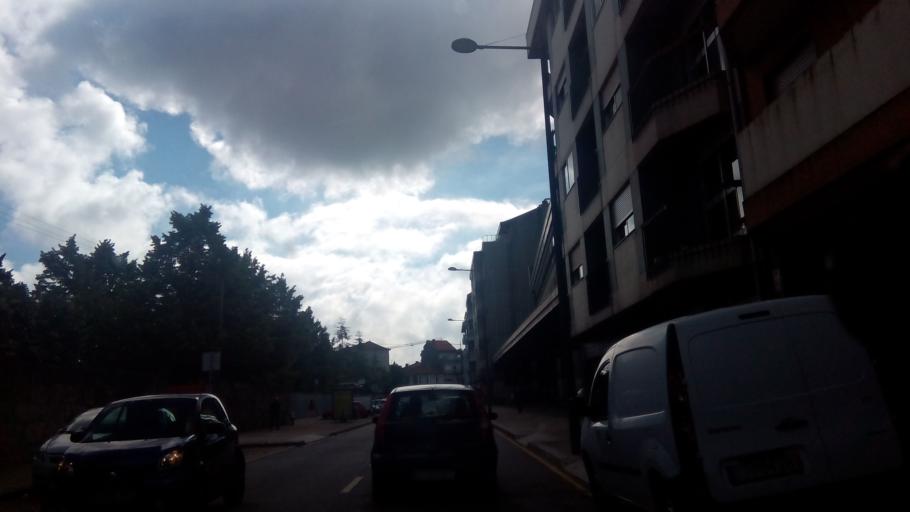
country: PT
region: Porto
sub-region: Porto
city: Porto
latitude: 41.1654
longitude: -8.6050
